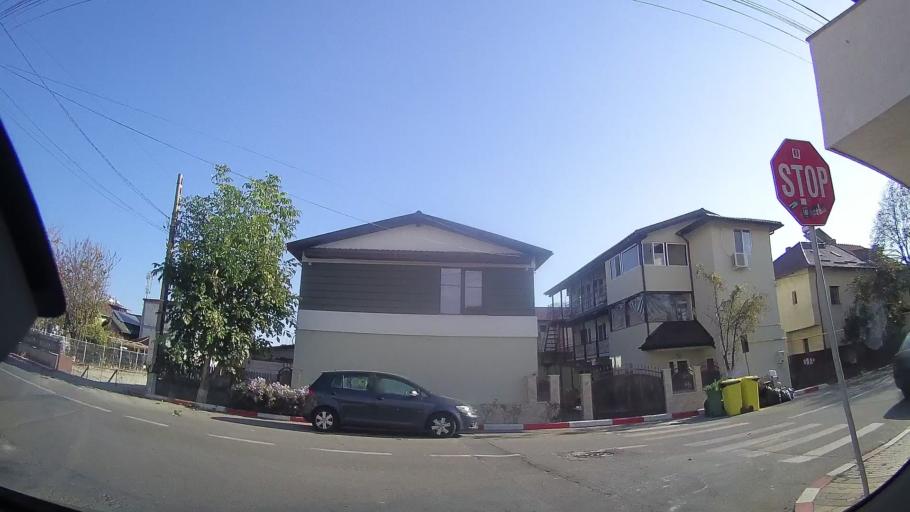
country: RO
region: Constanta
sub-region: Comuna Costinesti
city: Costinesti
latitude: 43.9532
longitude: 28.6342
